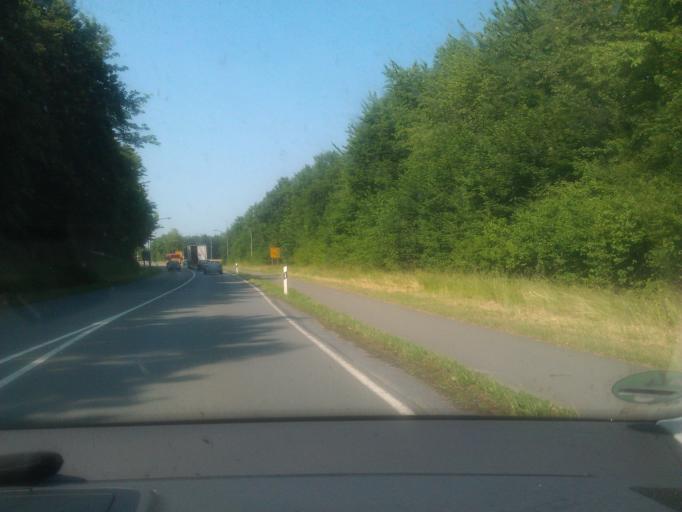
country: DE
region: North Rhine-Westphalia
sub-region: Regierungsbezirk Detmold
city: Leopoldshohe
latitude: 51.9973
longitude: 8.6960
